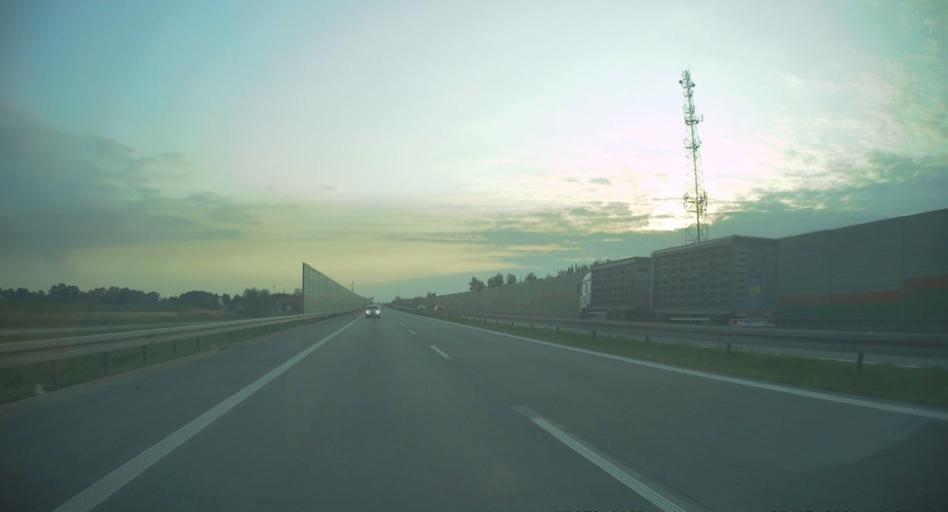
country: PL
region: Lodz Voivodeship
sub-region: Piotrkow Trybunalski
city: Piotrkow Trybunalski
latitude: 51.4431
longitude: 19.7000
